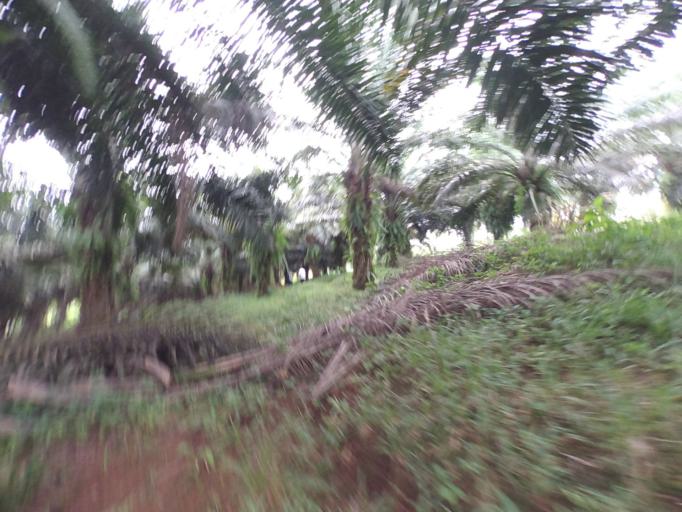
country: ID
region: West Java
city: Ciampea
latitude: -6.5508
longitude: 106.7158
